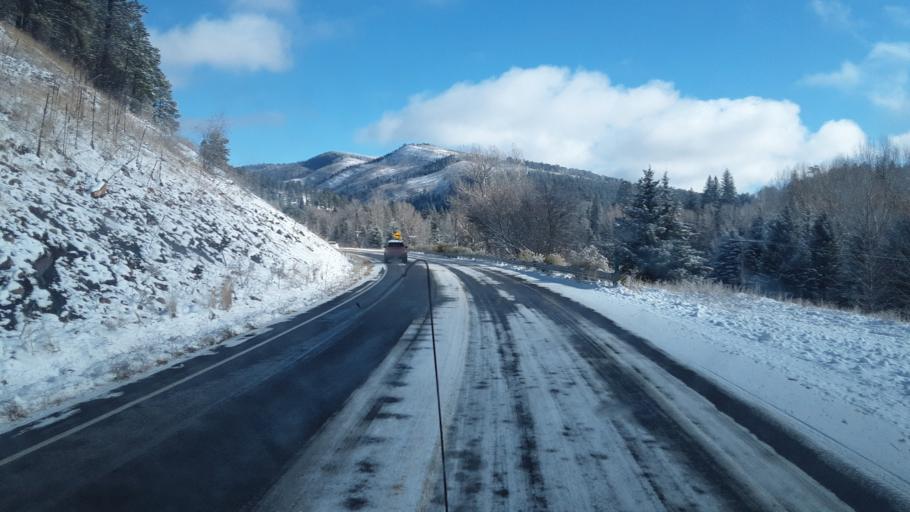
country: US
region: Colorado
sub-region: La Plata County
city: Bayfield
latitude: 37.3543
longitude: -107.6814
